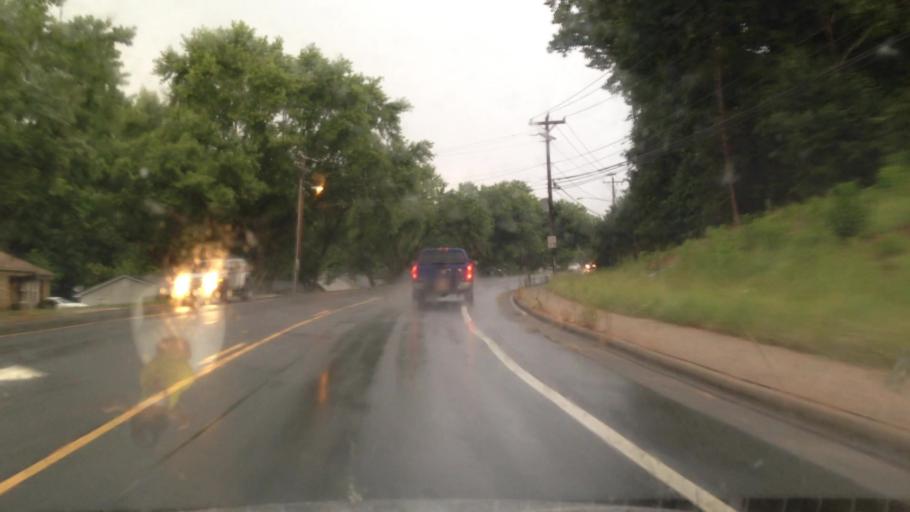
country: US
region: North Carolina
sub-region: Mecklenburg County
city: Pineville
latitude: 35.1346
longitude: -80.8959
